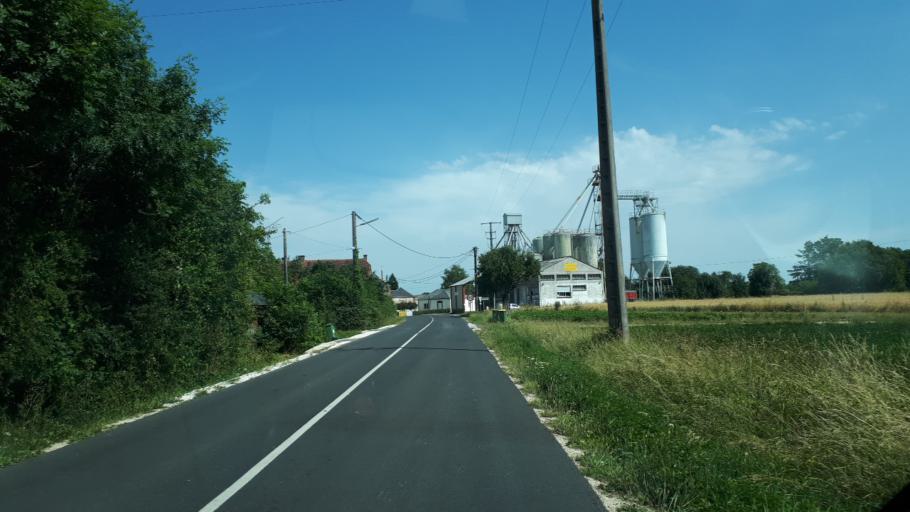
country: FR
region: Centre
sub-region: Departement du Loir-et-Cher
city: La Ville-aux-Clercs
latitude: 47.9555
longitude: 1.0805
